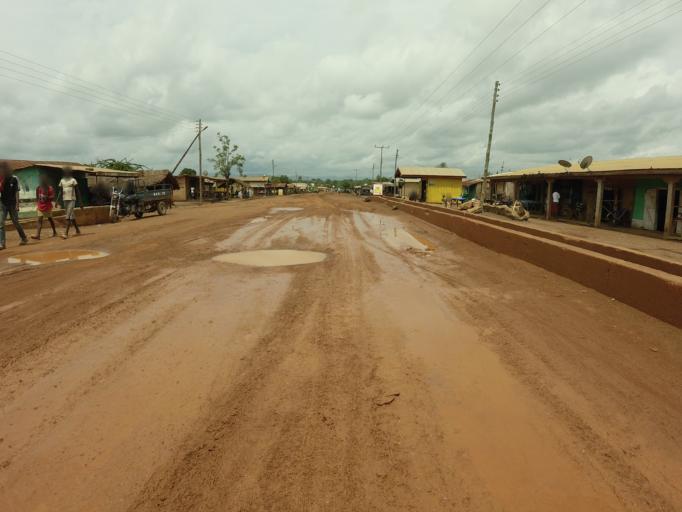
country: GH
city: Kpandae
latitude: 8.4003
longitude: 0.4057
